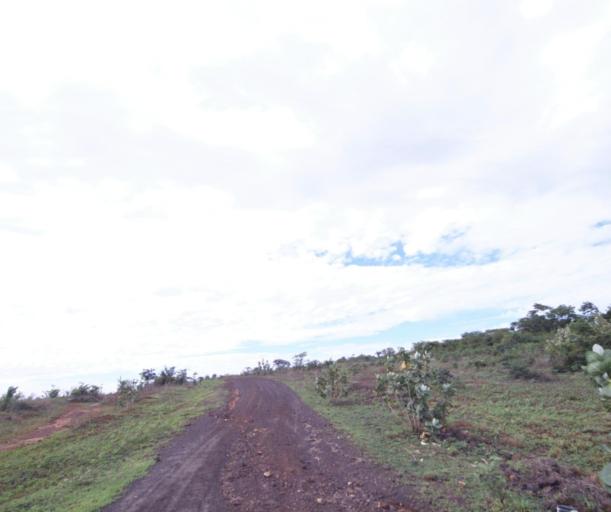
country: BR
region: Bahia
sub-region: Carinhanha
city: Carinhanha
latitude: -14.2221
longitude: -44.4405
